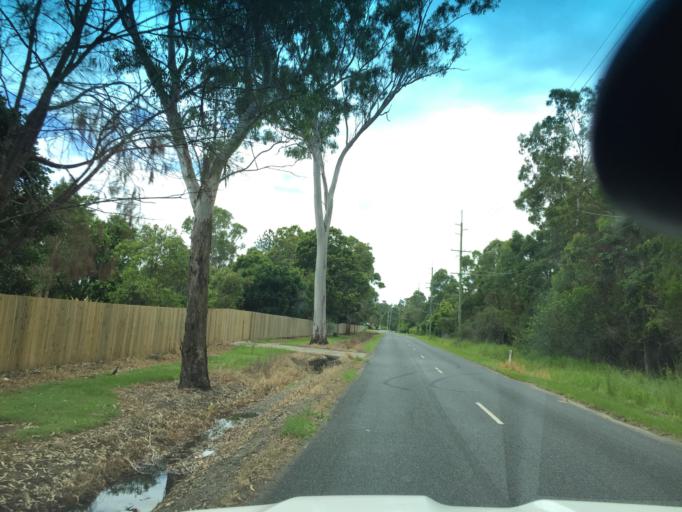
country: AU
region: Queensland
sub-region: Moreton Bay
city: Burpengary
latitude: -27.1714
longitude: 152.9847
